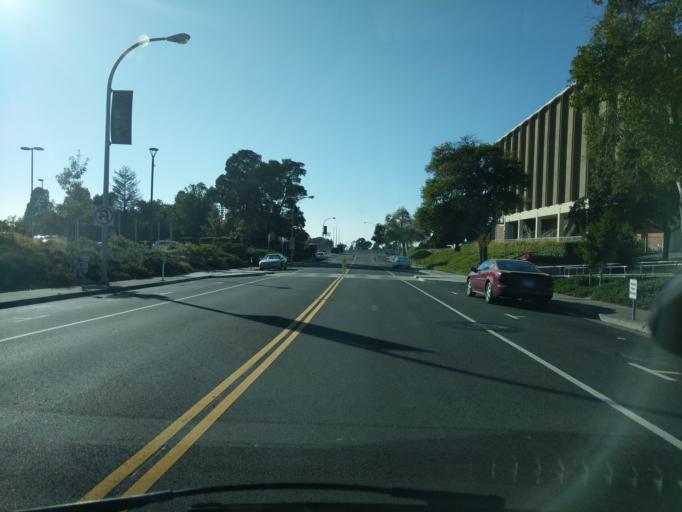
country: US
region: California
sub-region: Alameda County
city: Fairview
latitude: 37.6562
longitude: -122.0580
